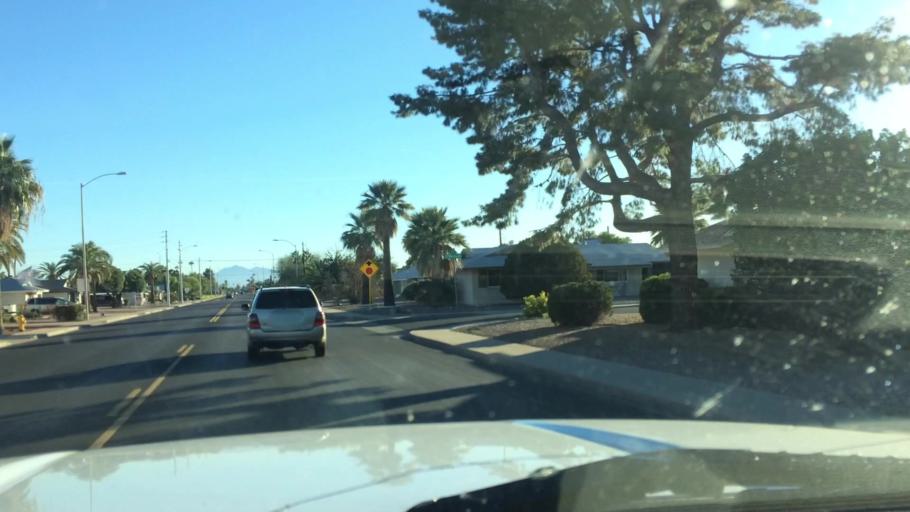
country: US
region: Arizona
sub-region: Maricopa County
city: Sun City
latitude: 33.5890
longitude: -112.2813
